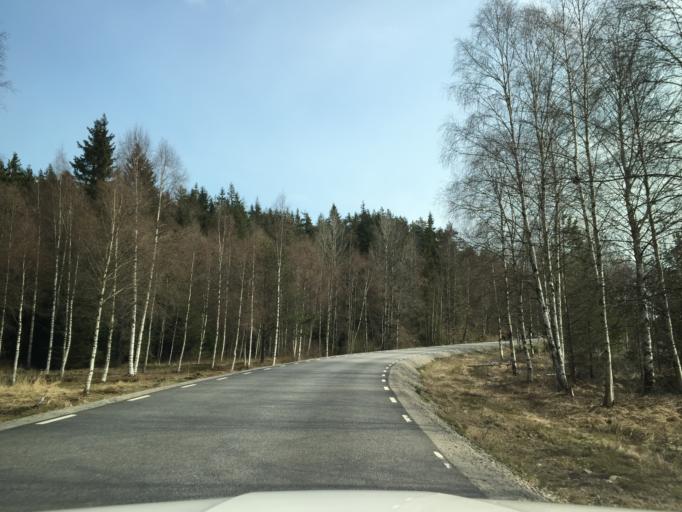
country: SE
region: Vaestra Goetaland
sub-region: Lilla Edets Kommun
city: Lilla Edet
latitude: 58.0884
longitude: 12.0381
